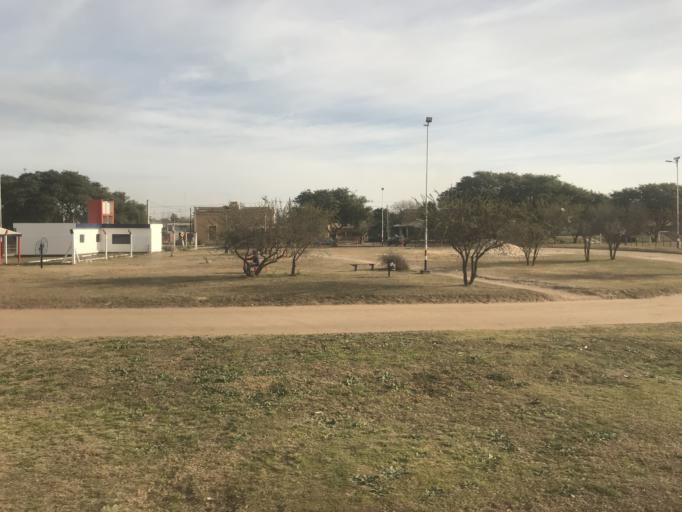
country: AR
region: Cordoba
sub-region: Departamento de Rio Segundo
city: Rio Segundo
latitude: -31.6553
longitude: -63.9090
